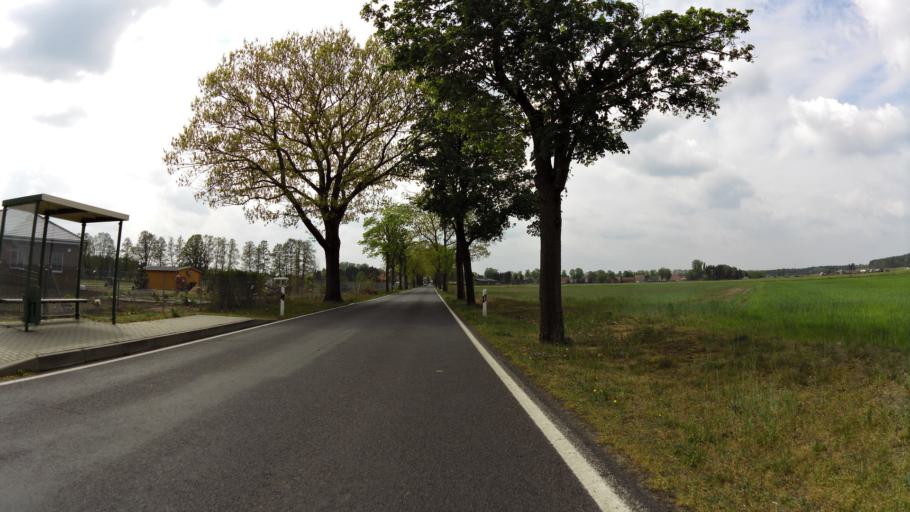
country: DE
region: Brandenburg
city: Bestensee
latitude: 52.2453
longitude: 13.7158
